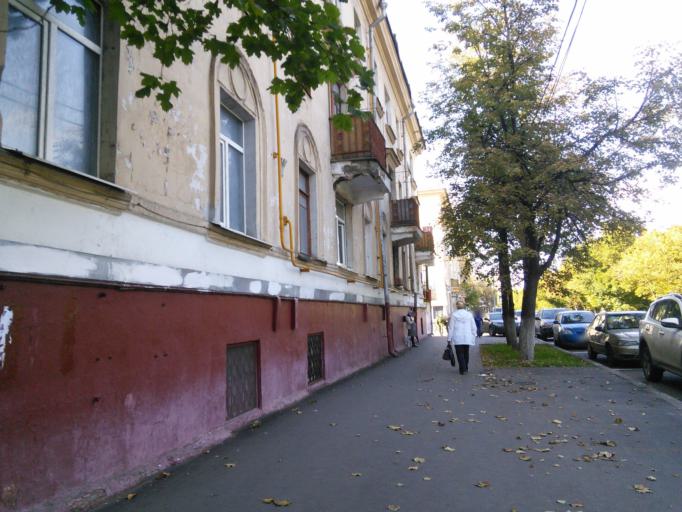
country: RU
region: Moskovskaya
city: Leninskiye Gory
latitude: 55.6882
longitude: 37.5711
